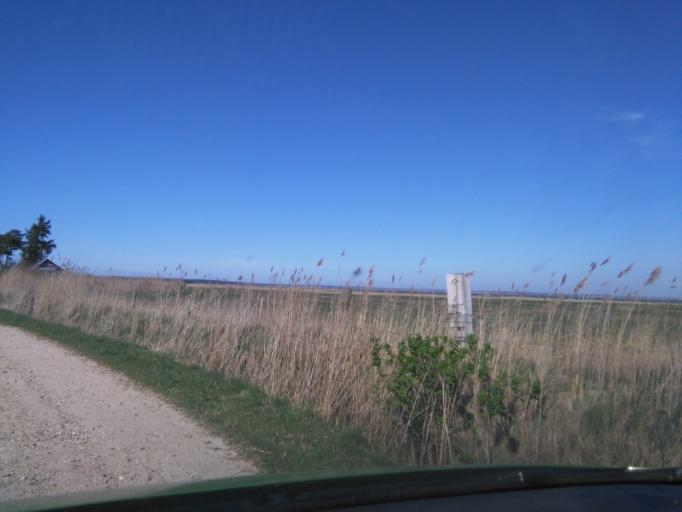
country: DK
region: South Denmark
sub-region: Varde Kommune
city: Oksbol
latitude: 55.5469
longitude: 8.2379
